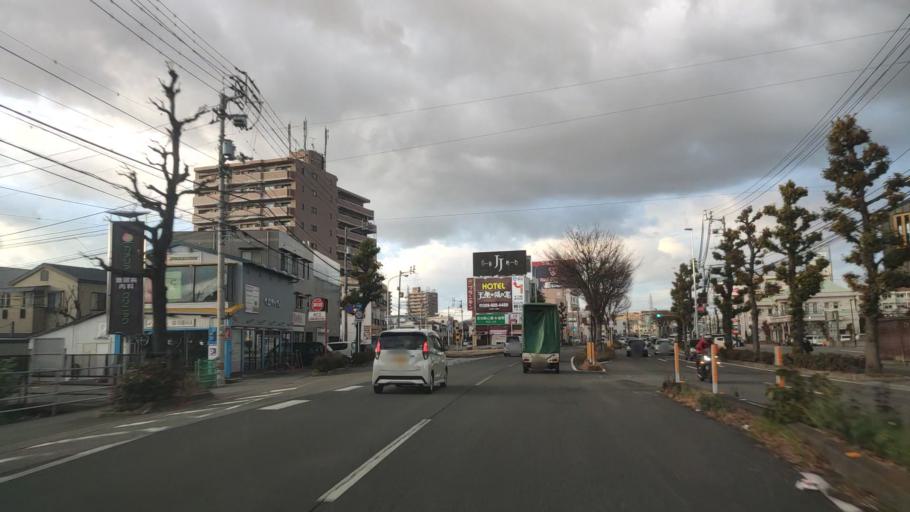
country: JP
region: Ehime
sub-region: Shikoku-chuo Shi
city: Matsuyama
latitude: 33.8153
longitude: 132.7773
